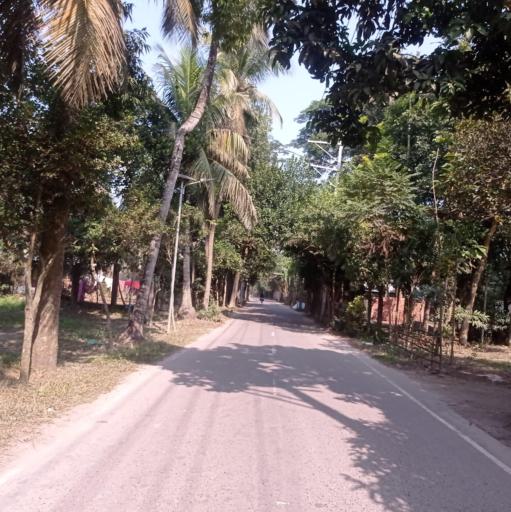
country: BD
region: Dhaka
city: Narsingdi
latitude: 24.0427
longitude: 90.6789
